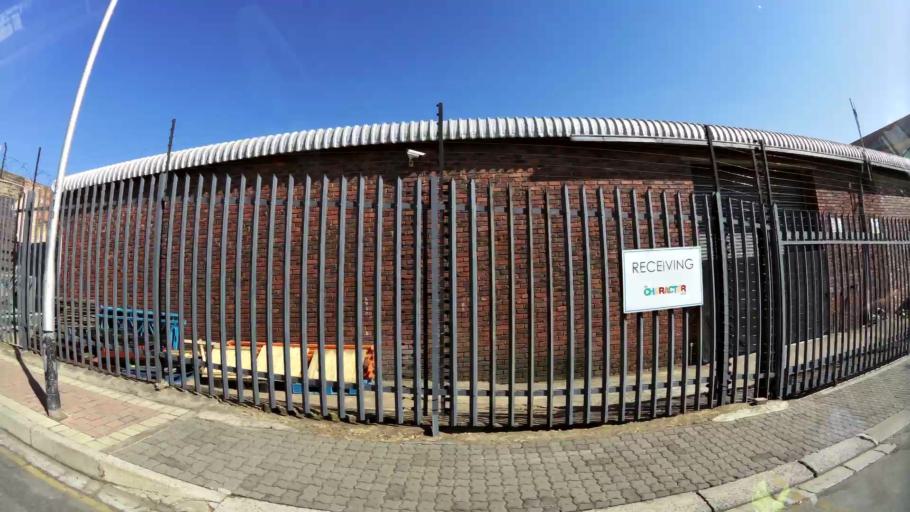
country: ZA
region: Gauteng
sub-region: City of Johannesburg Metropolitan Municipality
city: Johannesburg
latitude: -26.1979
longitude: 28.0658
